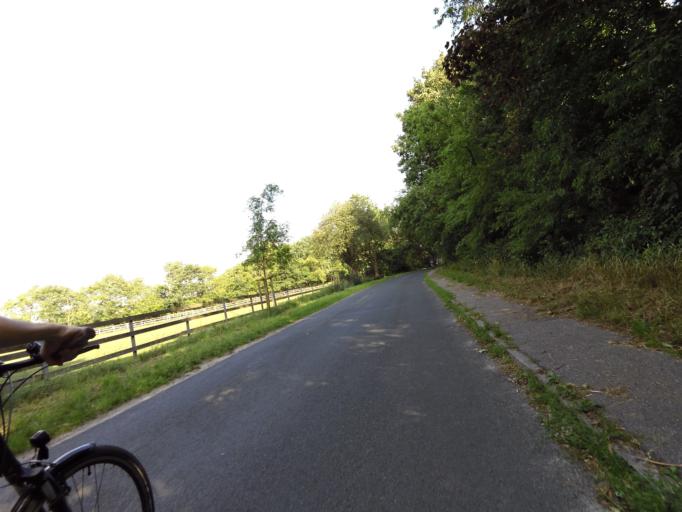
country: DE
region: Lower Saxony
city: Nordholz
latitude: 53.8264
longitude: 8.5854
